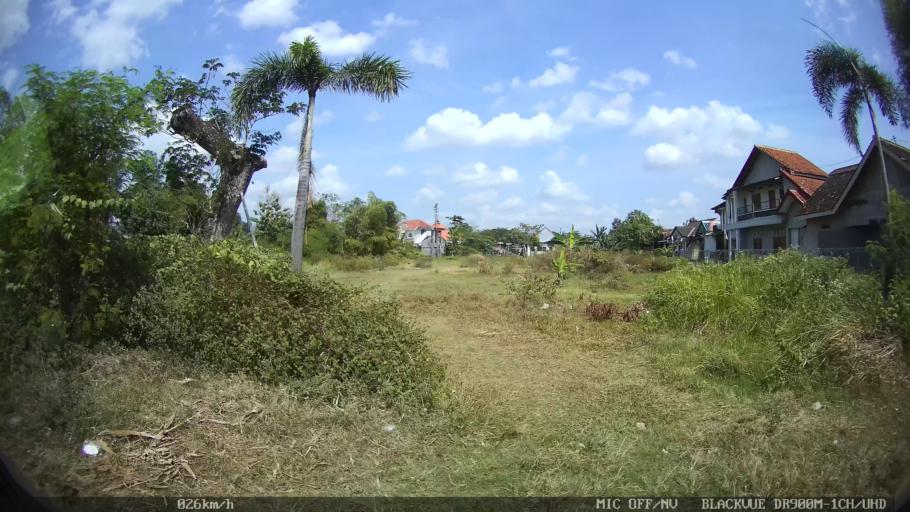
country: ID
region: Daerah Istimewa Yogyakarta
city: Sewon
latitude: -7.8316
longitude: 110.3781
